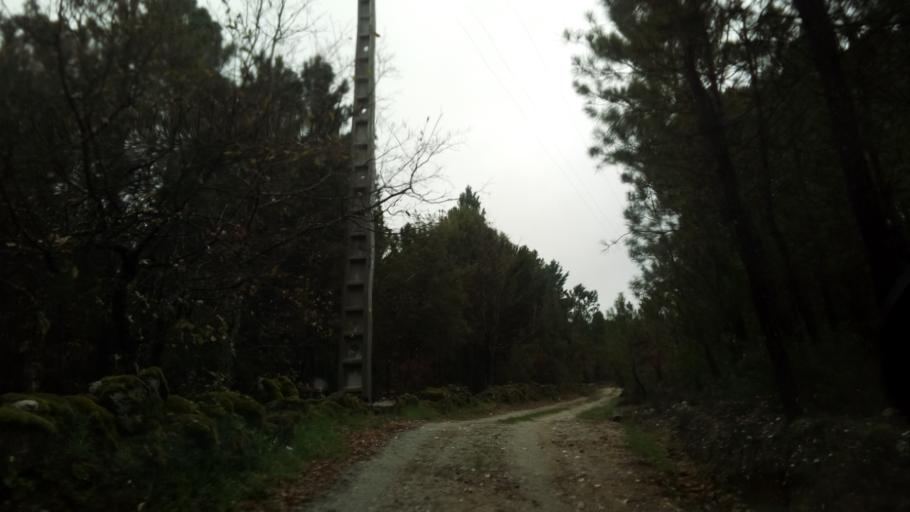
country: PT
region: Guarda
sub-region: Fornos de Algodres
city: Fornos de Algodres
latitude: 40.6224
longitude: -7.5237
